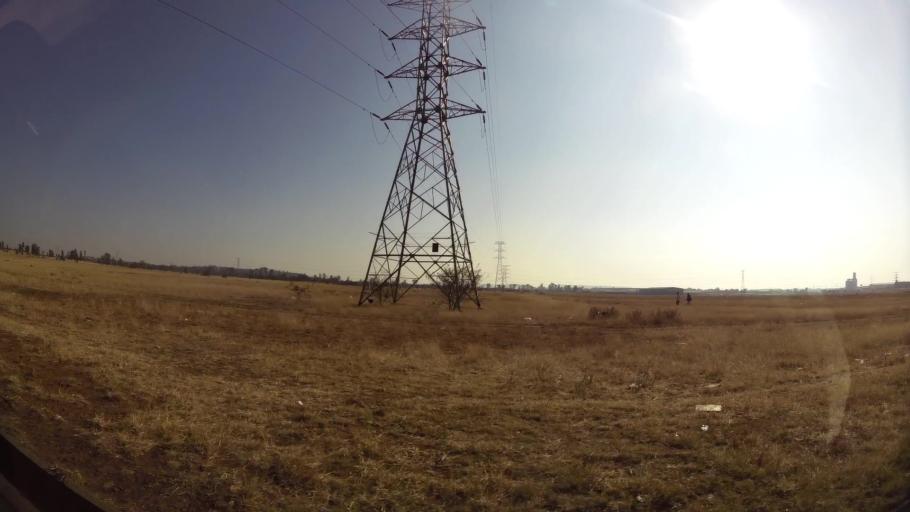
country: ZA
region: Orange Free State
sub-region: Mangaung Metropolitan Municipality
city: Bloemfontein
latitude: -29.1717
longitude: 26.2133
